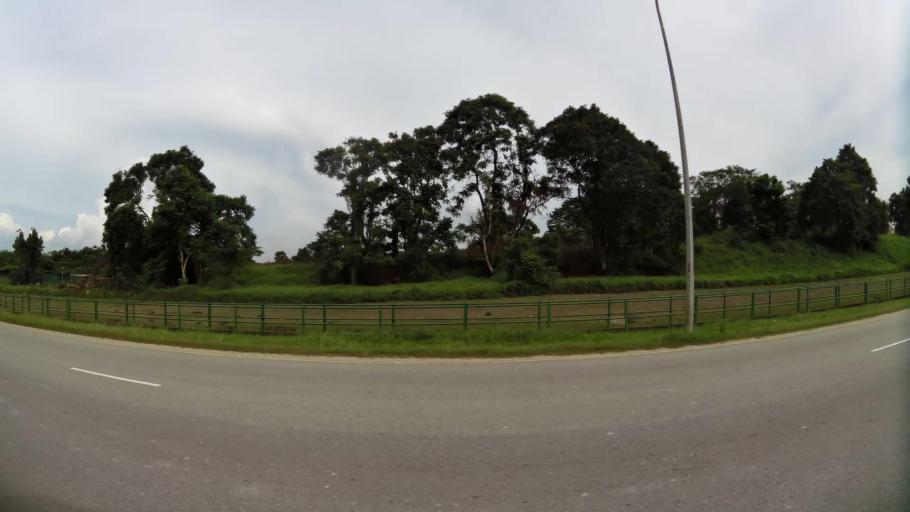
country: MY
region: Johor
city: Johor Bahru
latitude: 1.3838
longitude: 103.6973
